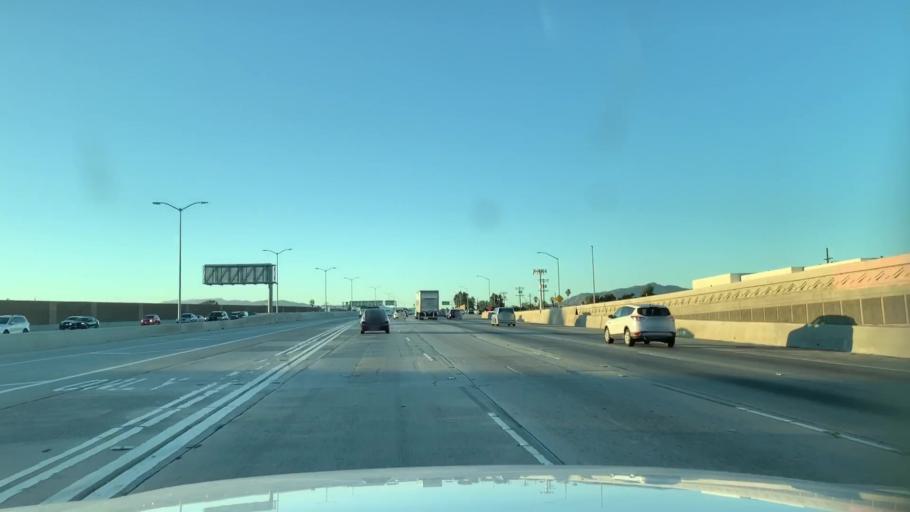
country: US
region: California
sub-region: Los Angeles County
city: San Fernando
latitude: 34.2360
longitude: -118.4128
